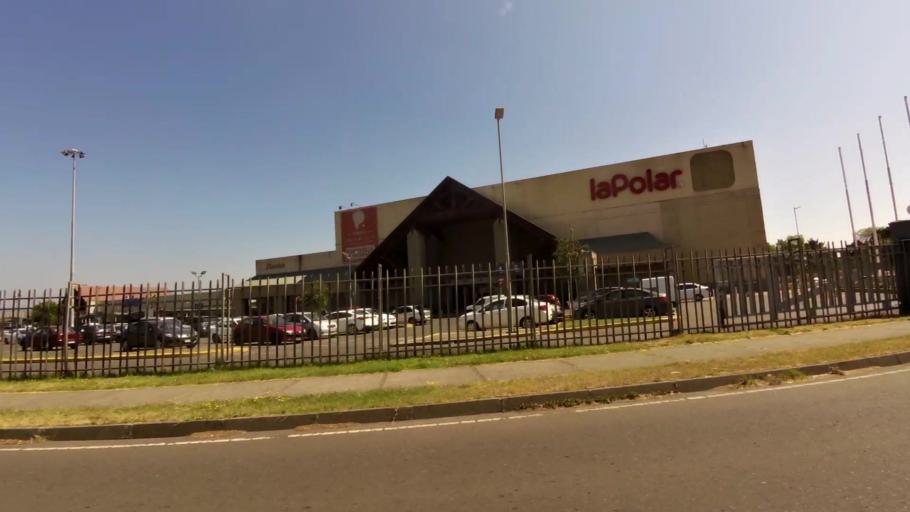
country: CL
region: Biobio
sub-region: Provincia de Concepcion
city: Concepcion
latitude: -36.7944
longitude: -73.0686
